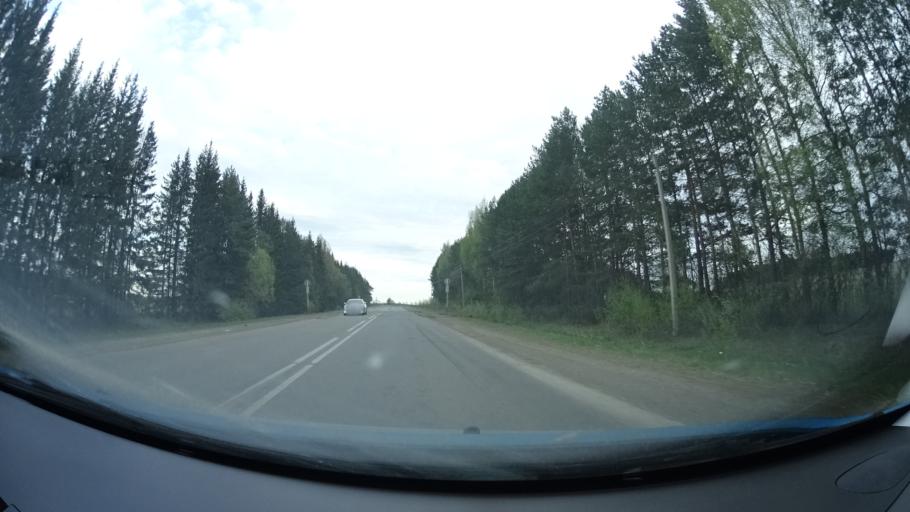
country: RU
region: Perm
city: Osa
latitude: 57.3183
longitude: 55.6207
